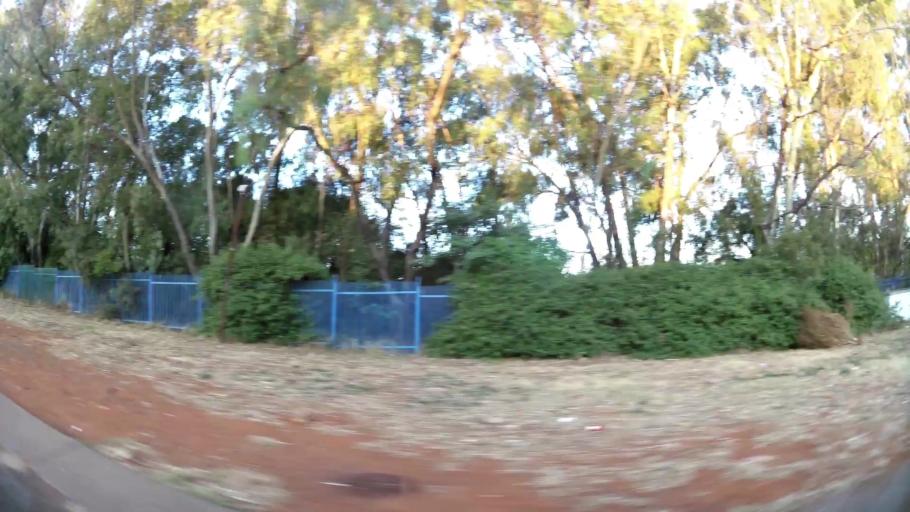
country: ZA
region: Gauteng
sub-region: City of Tshwane Metropolitan Municipality
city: Pretoria
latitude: -25.7383
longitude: 28.1419
